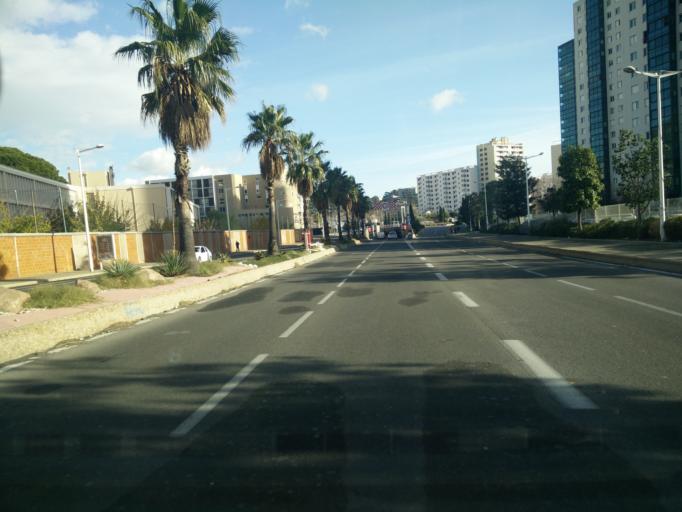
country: FR
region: Provence-Alpes-Cote d'Azur
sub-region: Departement du Var
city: Toulon
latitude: 43.1207
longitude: 5.9442
